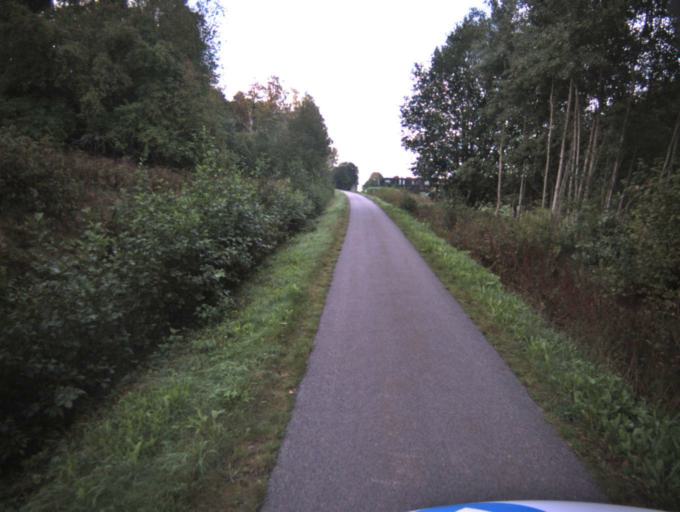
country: SE
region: Vaestra Goetaland
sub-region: Ulricehamns Kommun
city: Ulricehamn
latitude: 57.7669
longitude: 13.4006
